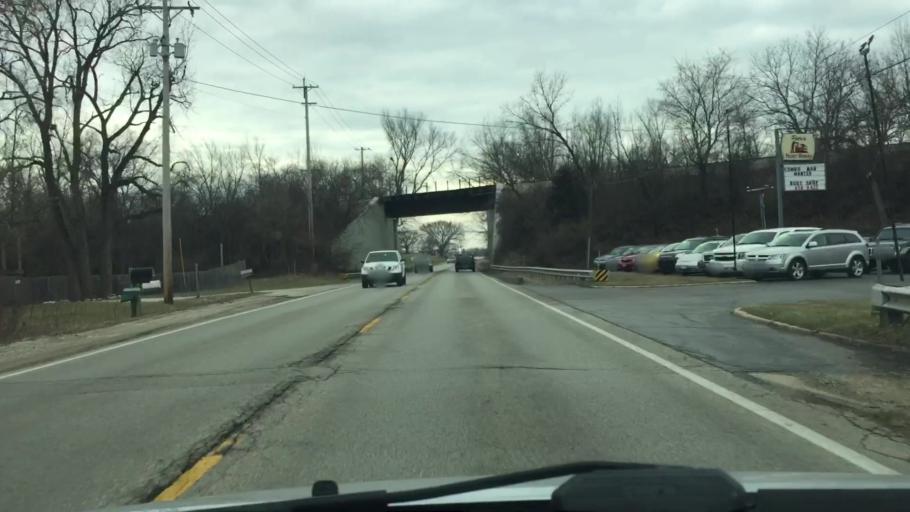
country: US
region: Illinois
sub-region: McHenry County
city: Richmond
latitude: 42.4571
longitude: -88.3060
